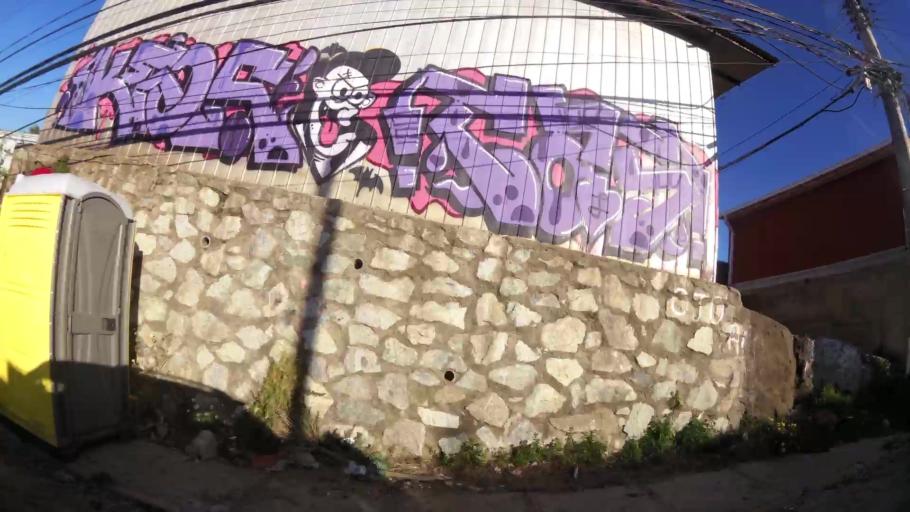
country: CL
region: Valparaiso
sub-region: Provincia de Valparaiso
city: Valparaiso
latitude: -33.0572
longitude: -71.6148
